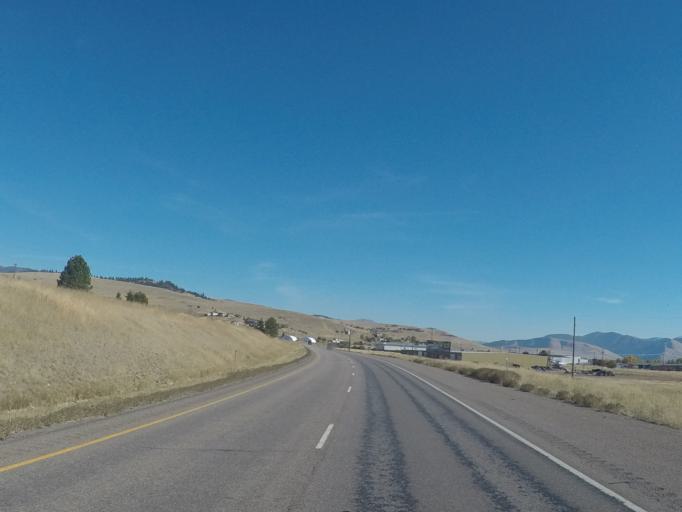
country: US
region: Montana
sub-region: Missoula County
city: Orchard Homes
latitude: 46.9386
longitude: -114.1076
